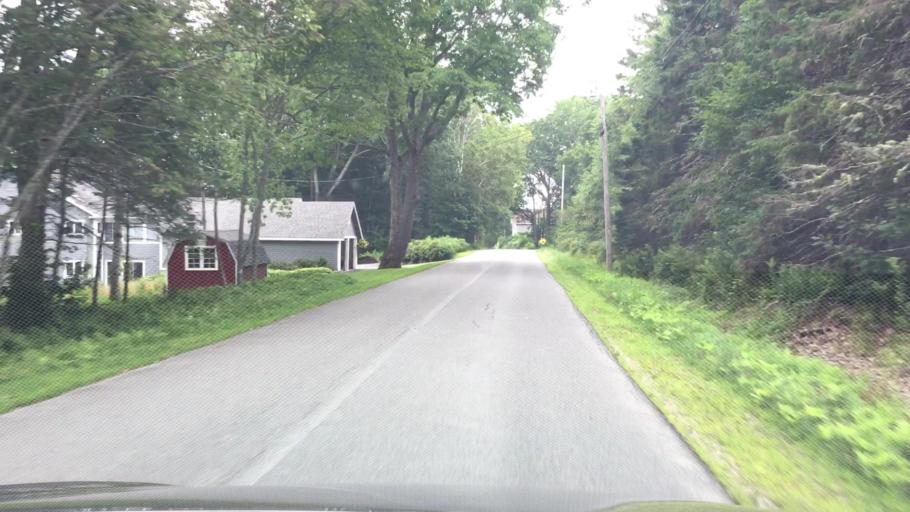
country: US
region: Maine
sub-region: Waldo County
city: Stockton Springs
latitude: 44.5097
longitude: -68.8105
